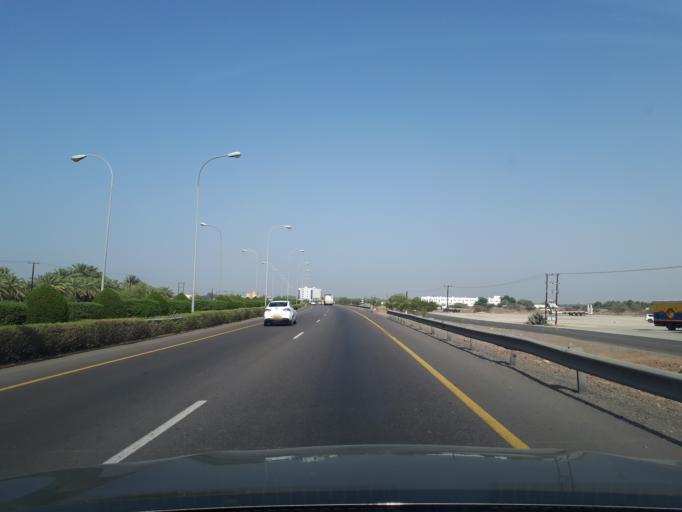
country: OM
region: Al Batinah
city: Al Sohar
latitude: 24.4119
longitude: 56.6370
